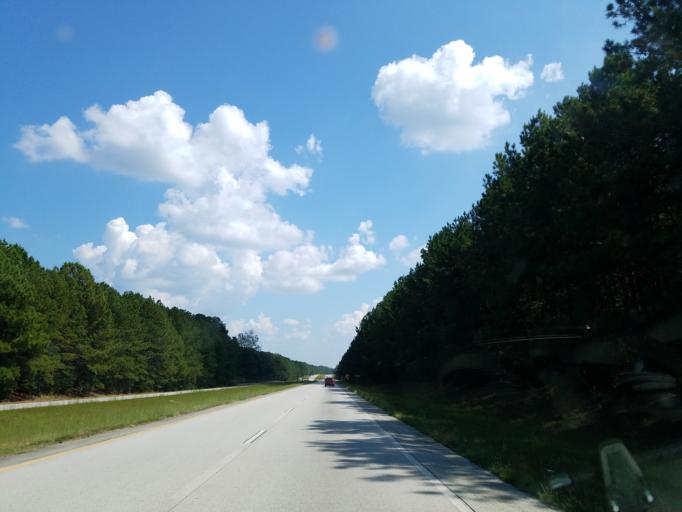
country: US
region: Georgia
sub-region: Oconee County
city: Bogart
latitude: 33.9369
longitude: -83.5449
